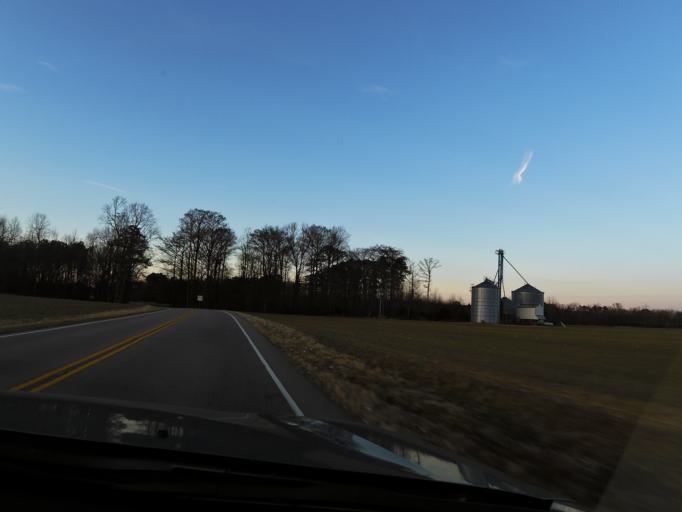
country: US
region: Virginia
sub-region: Southampton County
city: Courtland
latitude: 36.7324
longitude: -77.0735
